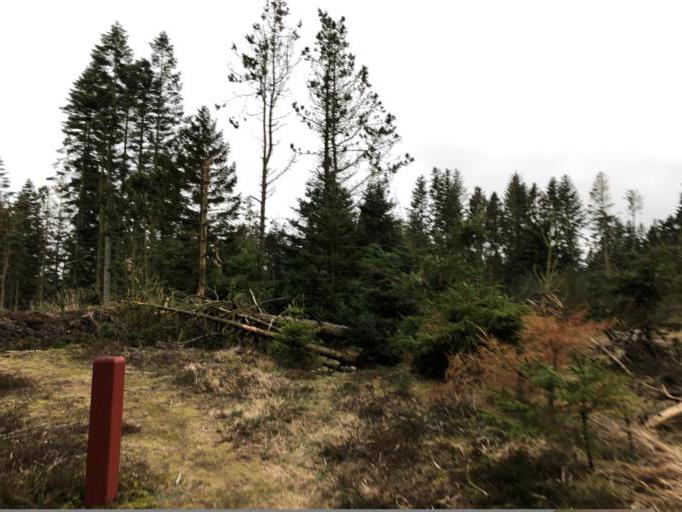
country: DK
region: Central Jutland
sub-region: Holstebro Kommune
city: Ulfborg
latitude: 56.2685
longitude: 8.4607
